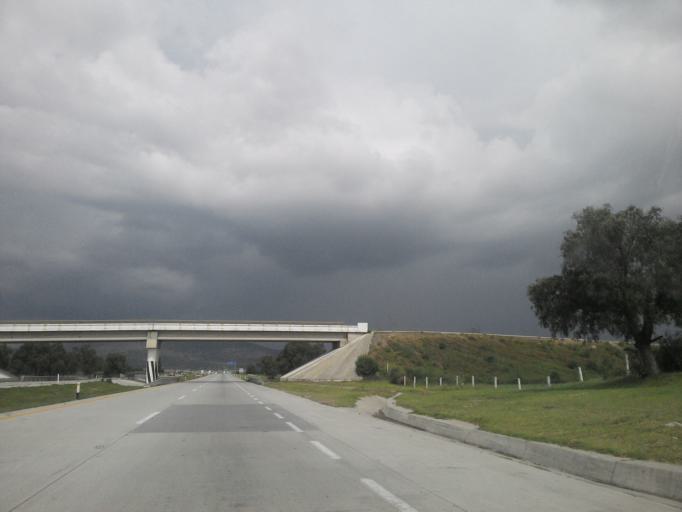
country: MX
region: Mexico
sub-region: Hueypoxtla
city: Santa Maria Ajoloapan
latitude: 19.9591
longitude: -99.0710
